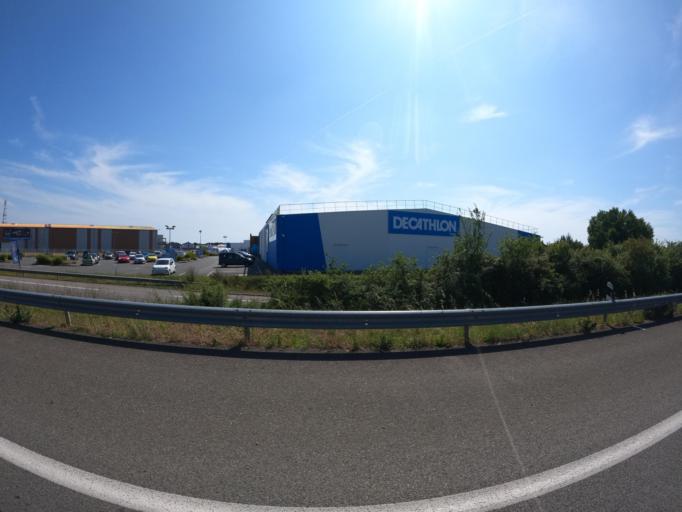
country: FR
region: Pays de la Loire
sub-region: Departement de la Loire-Atlantique
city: Pornic
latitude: 47.1276
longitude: -2.1162
